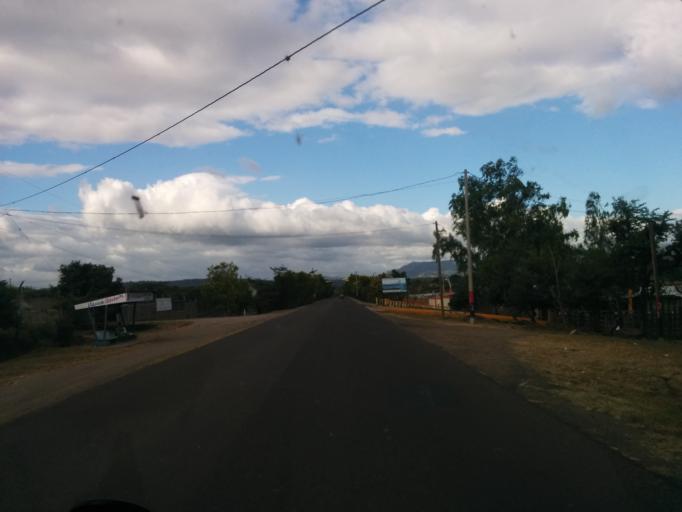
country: NI
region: Esteli
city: Esteli
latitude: 13.1675
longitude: -86.3675
